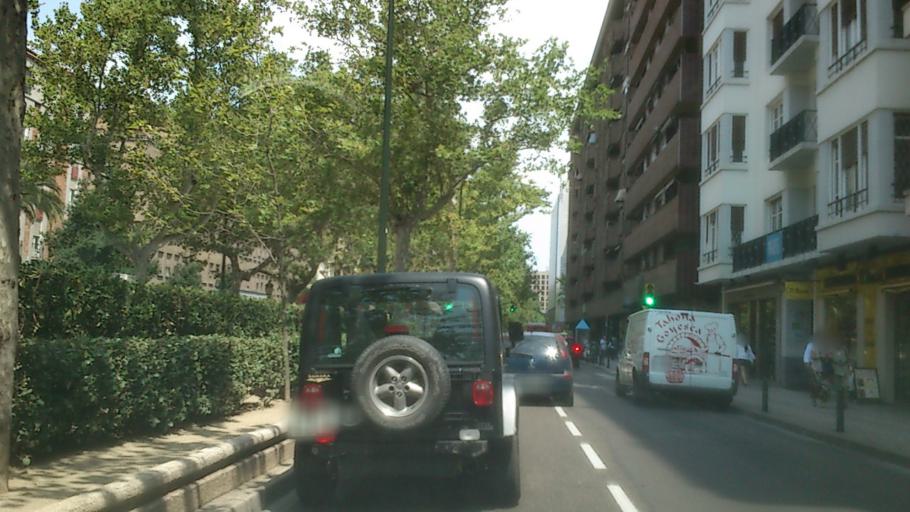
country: ES
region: Aragon
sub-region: Provincia de Zaragoza
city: Zaragoza
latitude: 41.6434
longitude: -0.8862
